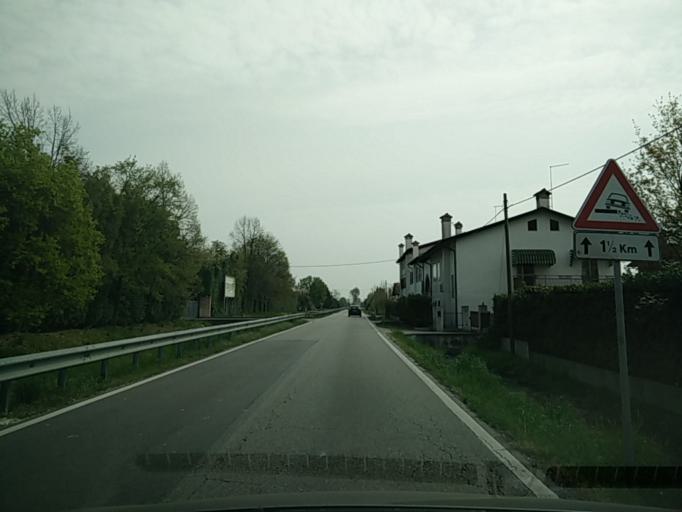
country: IT
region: Veneto
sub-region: Provincia di Venezia
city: Caltana
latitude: 45.4774
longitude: 12.0393
